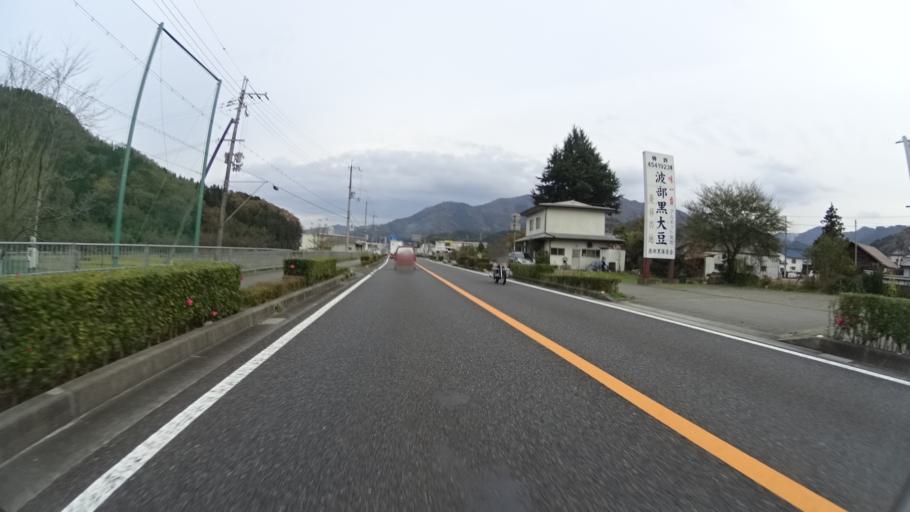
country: JP
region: Hyogo
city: Sasayama
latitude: 35.0695
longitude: 135.2816
